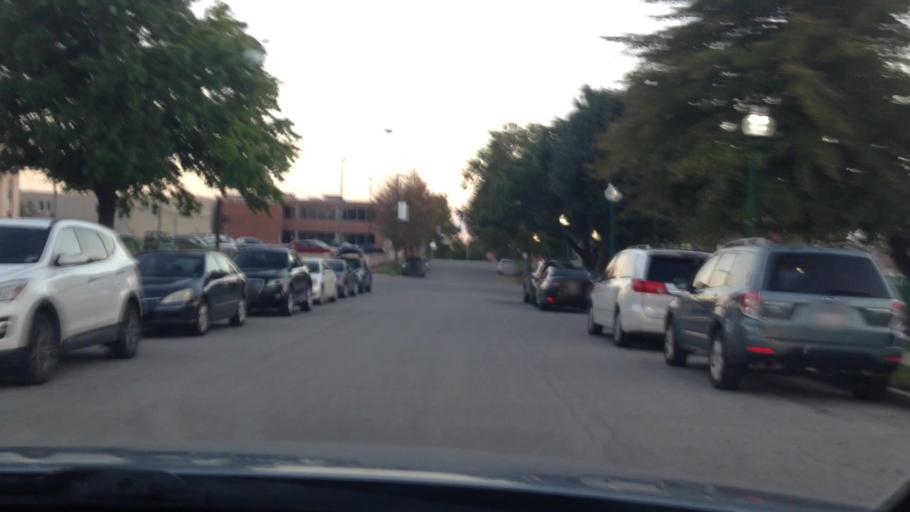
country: US
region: Kansas
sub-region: Johnson County
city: Westwood
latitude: 39.0554
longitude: -94.5873
